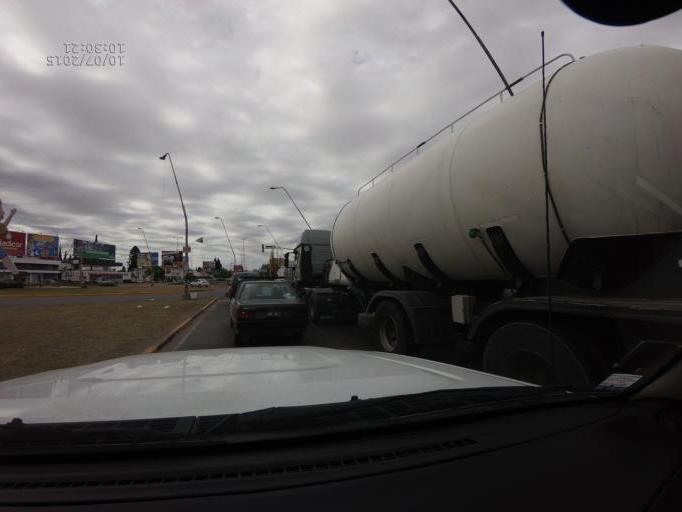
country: AR
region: Cordoba
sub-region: Departamento de Capital
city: Cordoba
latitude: -31.3581
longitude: -64.2404
